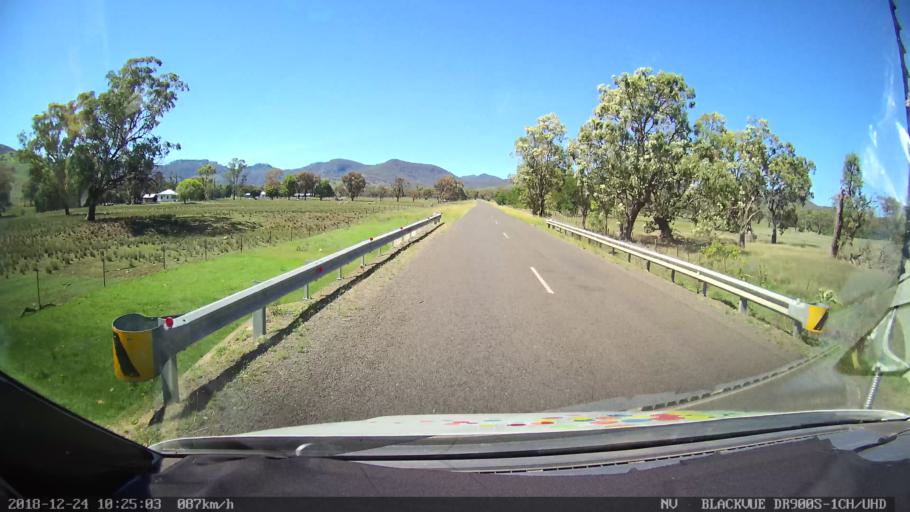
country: AU
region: New South Wales
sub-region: Liverpool Plains
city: Quirindi
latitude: -31.7941
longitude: 150.5302
